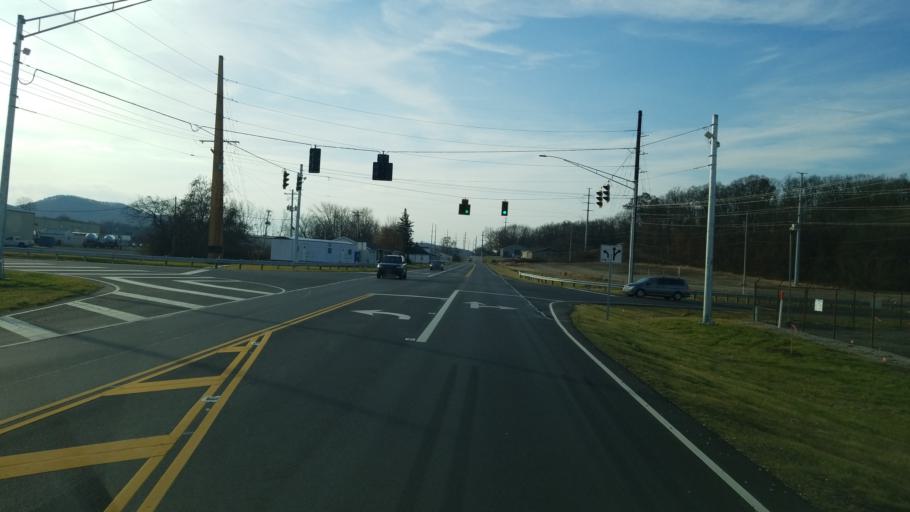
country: US
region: Ohio
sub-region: Ross County
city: Chillicothe
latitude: 39.4076
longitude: -82.9596
